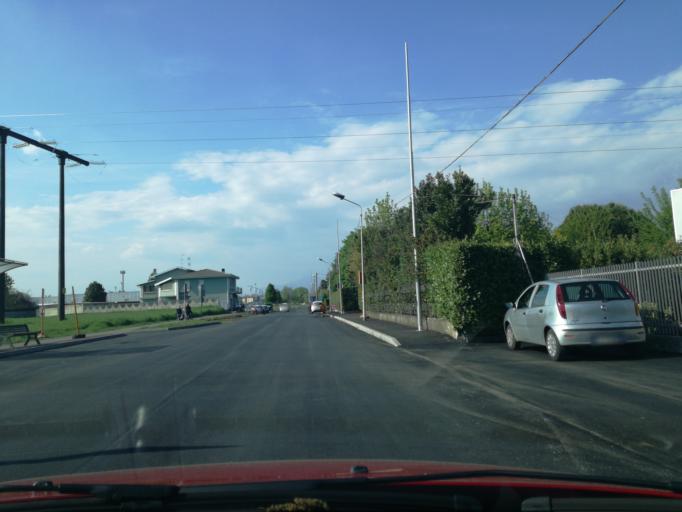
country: IT
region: Lombardy
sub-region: Provincia di Monza e Brianza
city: Cornate d'Adda
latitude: 45.6361
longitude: 9.4715
